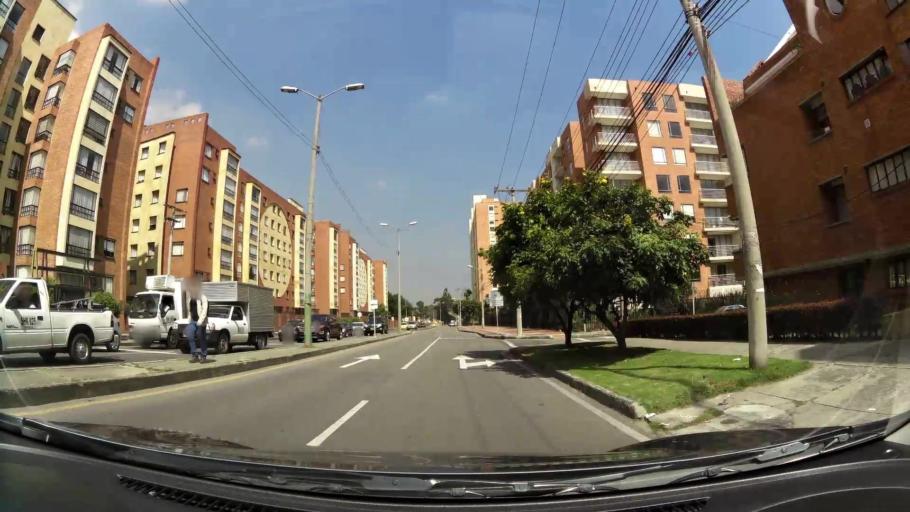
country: CO
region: Bogota D.C.
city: Barrio San Luis
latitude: 4.6858
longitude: -74.0367
